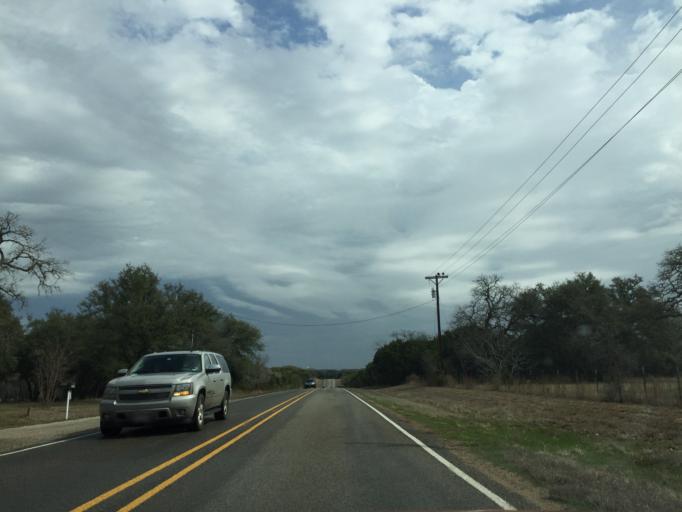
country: US
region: Texas
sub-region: Williamson County
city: Leander
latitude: 30.6577
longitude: -97.9571
